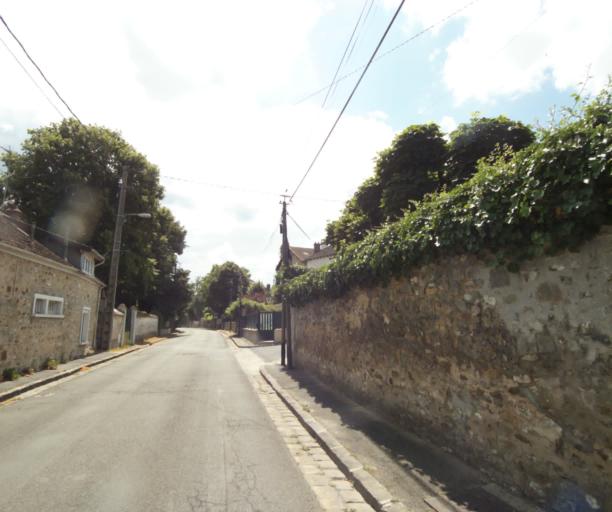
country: FR
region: Ile-de-France
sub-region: Departement de Seine-et-Marne
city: Bois-le-Roi
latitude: 48.4673
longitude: 2.7096
